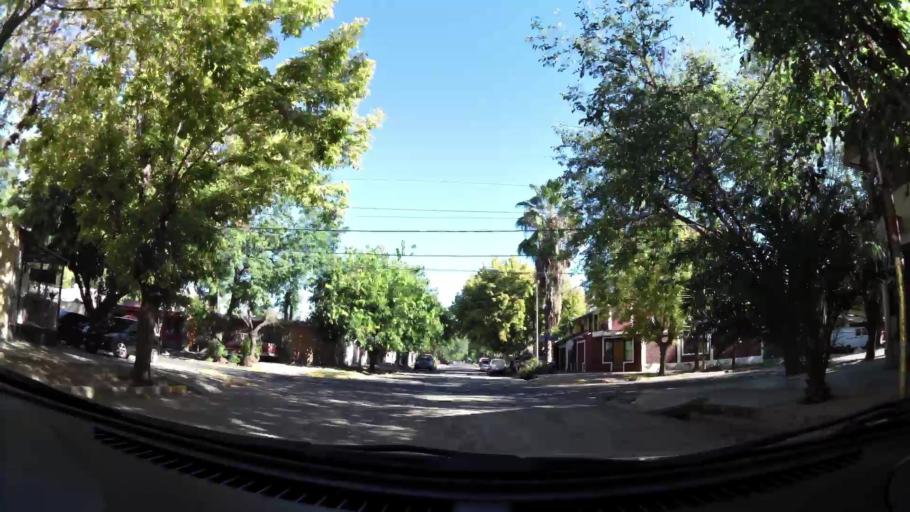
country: AR
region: Mendoza
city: Las Heras
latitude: -32.8517
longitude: -68.8278
